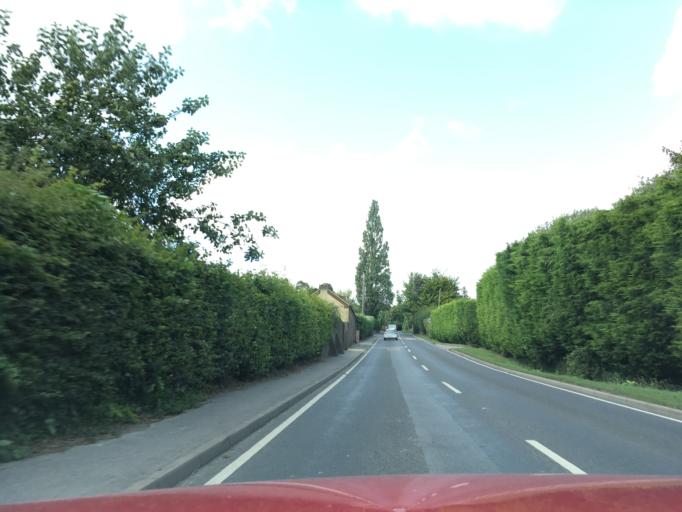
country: GB
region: England
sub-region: Kent
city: Headcorn
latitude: 51.2102
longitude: 0.5901
